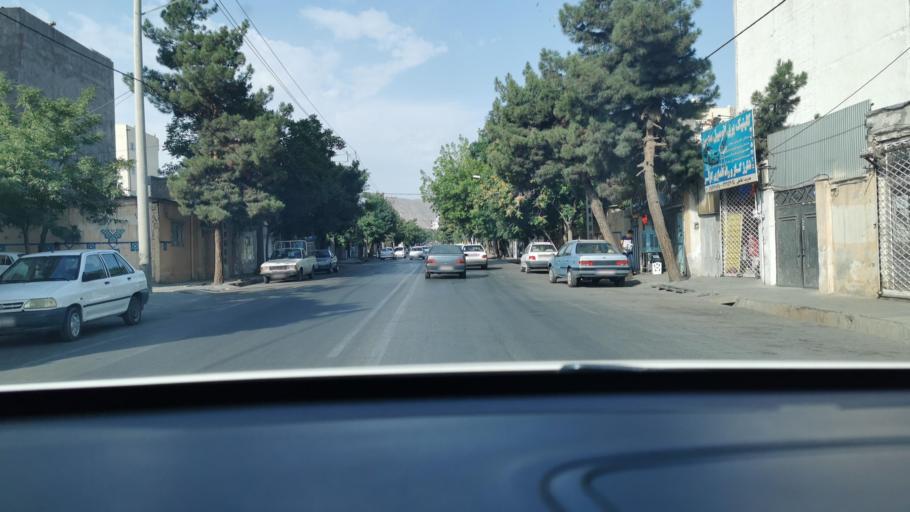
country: IR
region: Razavi Khorasan
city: Mashhad
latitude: 36.2600
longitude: 59.6145
